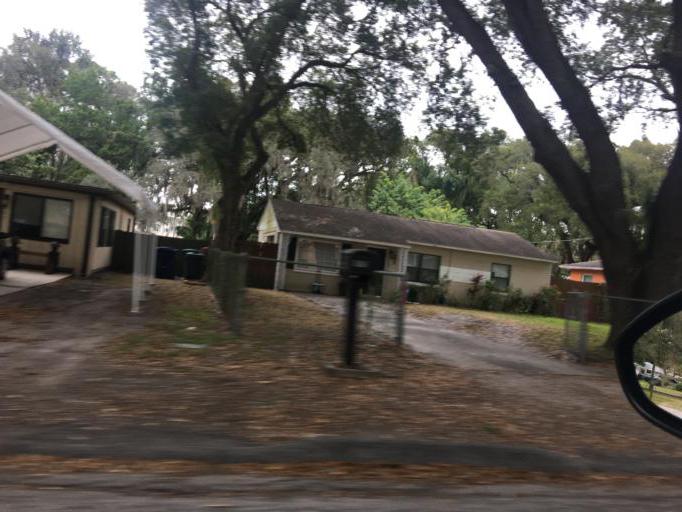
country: US
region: Florida
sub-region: Hillsborough County
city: Carrollwood
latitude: 28.0368
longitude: -82.4659
